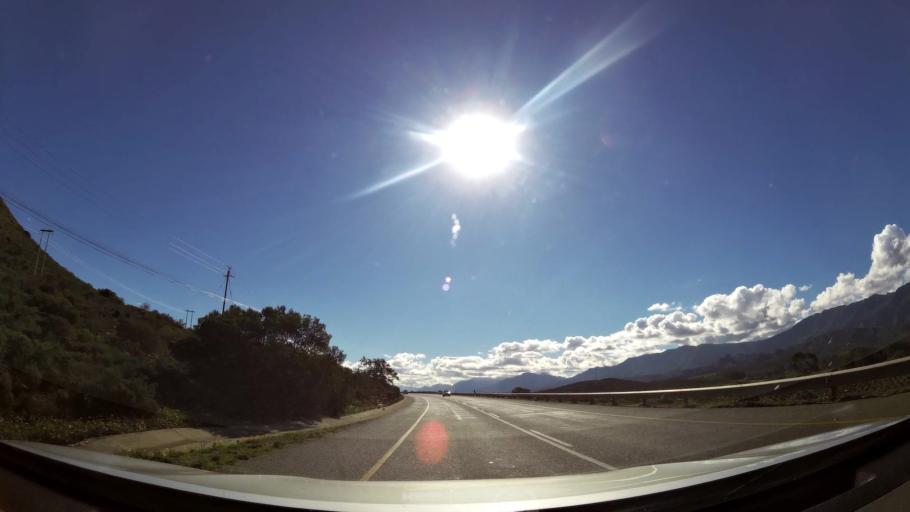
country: ZA
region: Western Cape
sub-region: Cape Winelands District Municipality
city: Ashton
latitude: -33.7798
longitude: 19.7659
